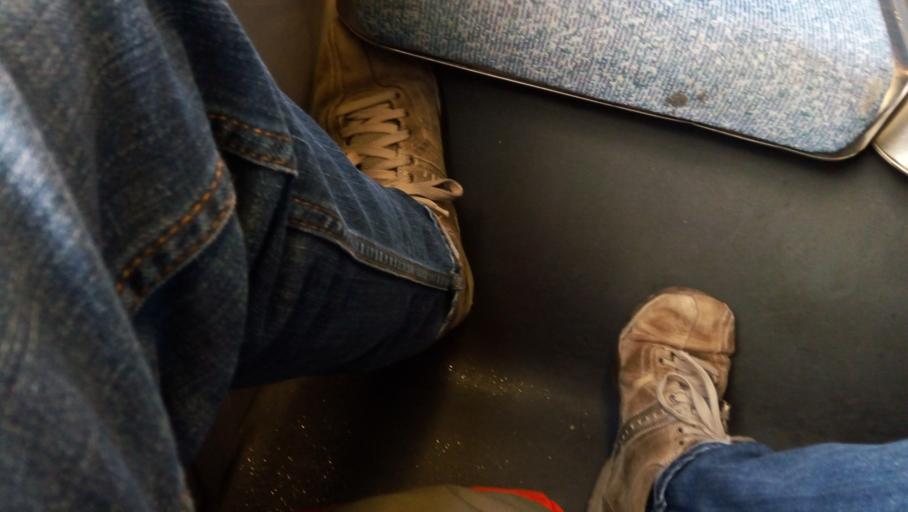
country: CA
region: British Columbia
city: Victoria
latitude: 48.4279
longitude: -123.3645
